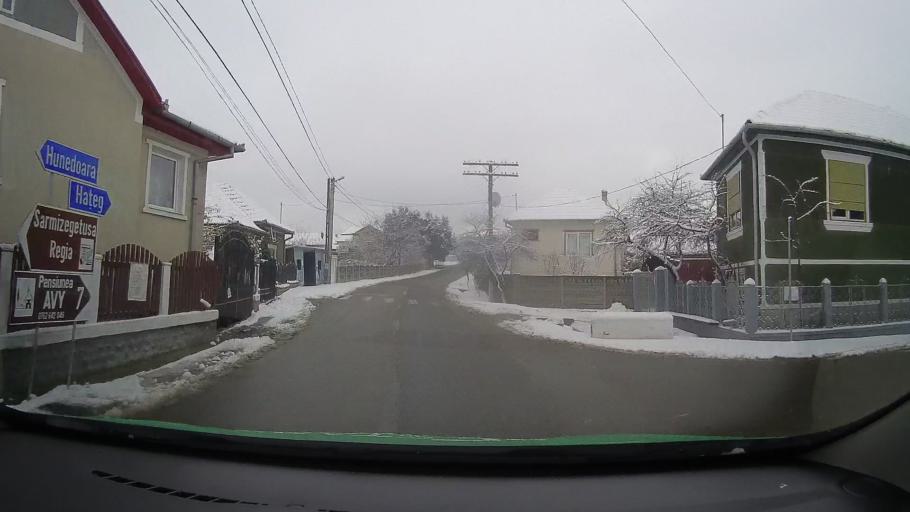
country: RO
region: Hunedoara
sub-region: Oras Hateg
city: Hateg
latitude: 45.6517
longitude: 22.9261
